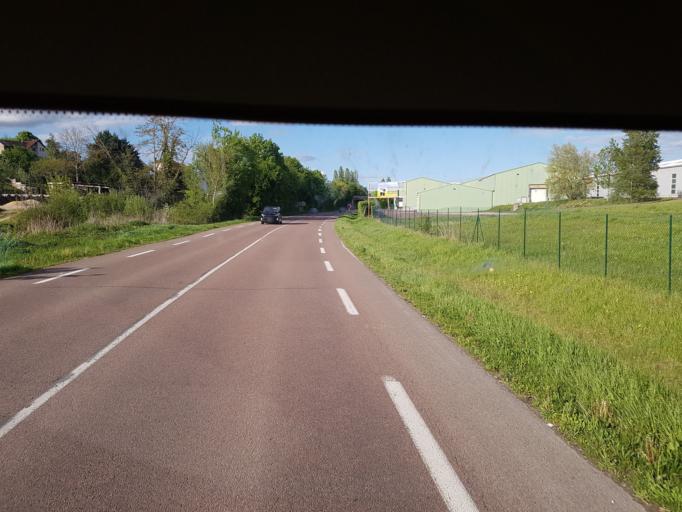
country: FR
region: Bourgogne
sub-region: Departement de l'Yonne
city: Saint-Florentin
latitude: 48.0026
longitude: 3.7365
